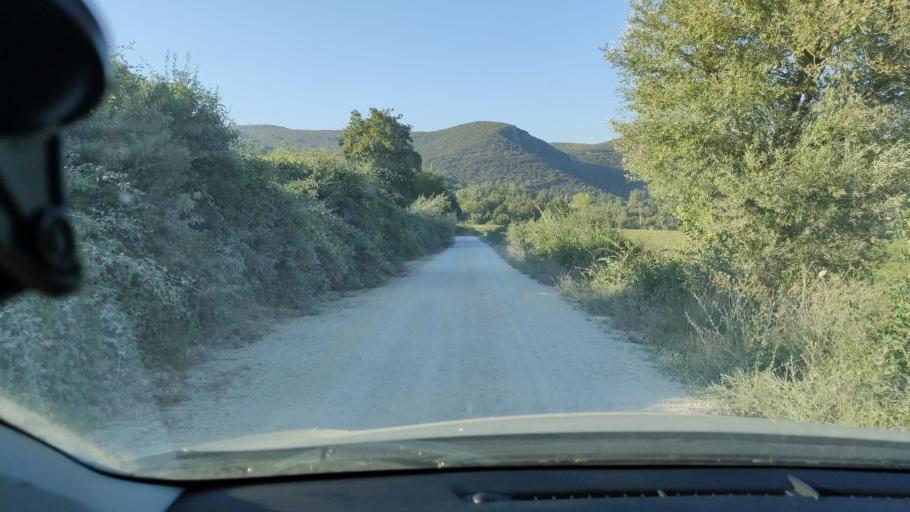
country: IT
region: Umbria
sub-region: Provincia di Terni
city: Amelia
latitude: 42.5419
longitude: 12.3861
